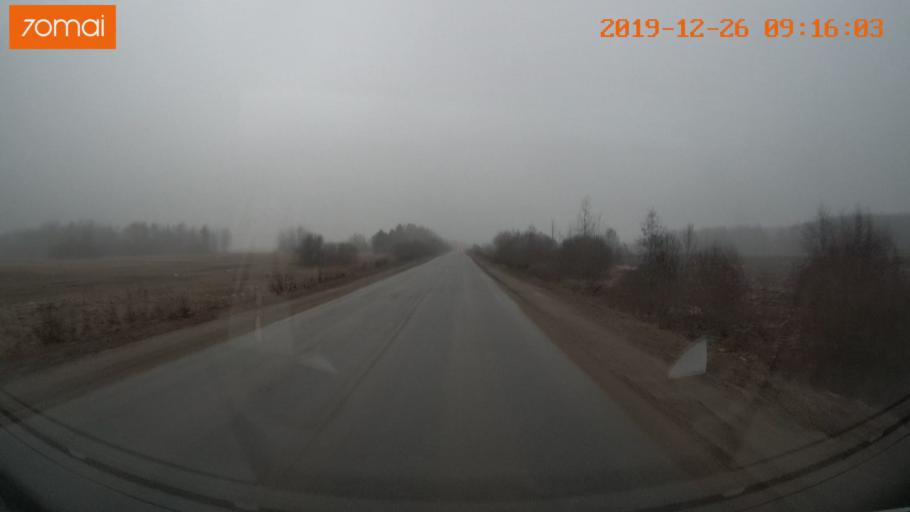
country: RU
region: Vologda
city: Gryazovets
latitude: 58.9137
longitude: 40.2390
